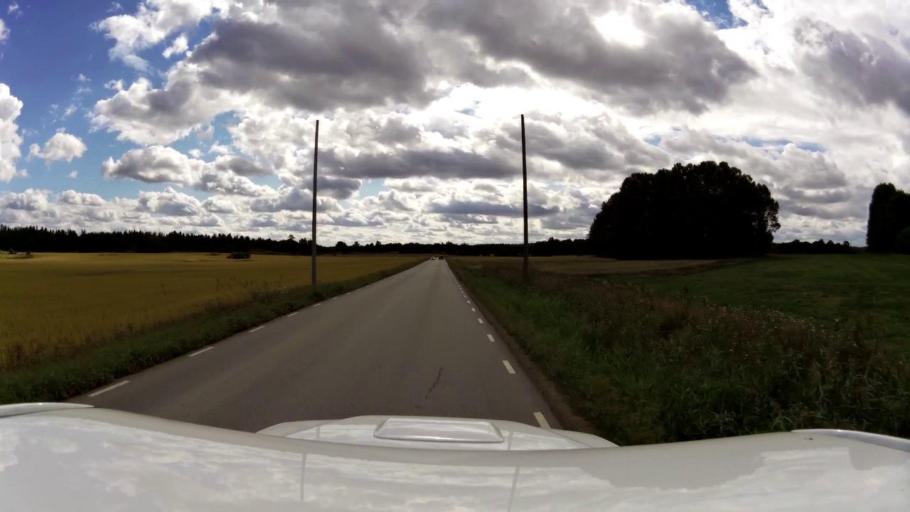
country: SE
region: OEstergoetland
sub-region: Linkopings Kommun
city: Linkoping
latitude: 58.3793
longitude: 15.5945
